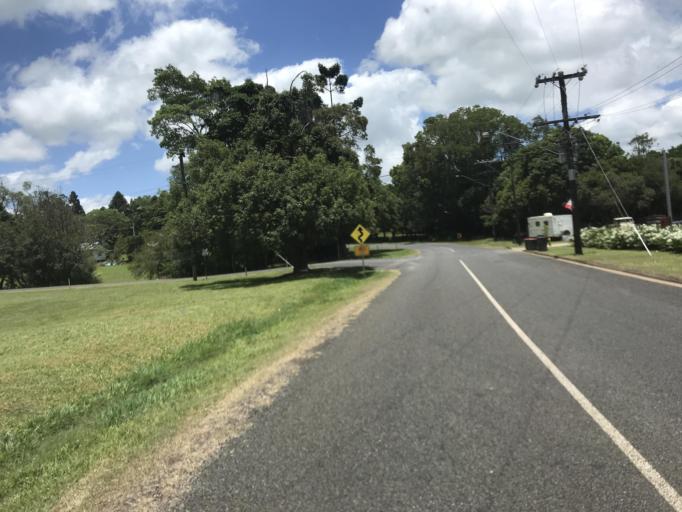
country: AU
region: Queensland
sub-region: Tablelands
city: Atherton
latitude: -17.3449
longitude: 145.5952
